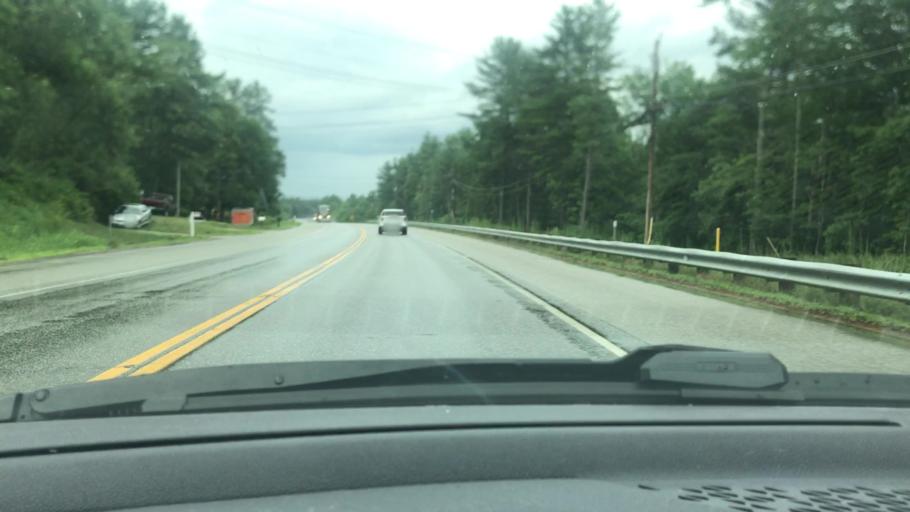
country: US
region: New Hampshire
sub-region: Merrimack County
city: Chichester
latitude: 43.2641
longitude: -71.4577
